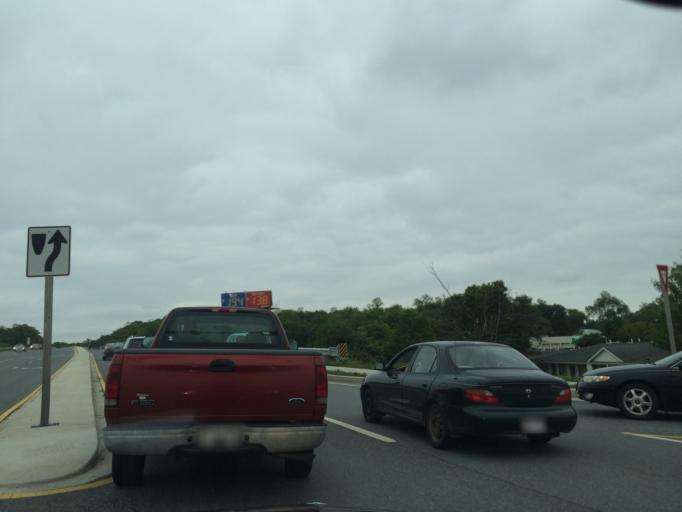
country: US
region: Maryland
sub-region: Washington County
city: Halfway
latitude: 39.6269
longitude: -77.7665
